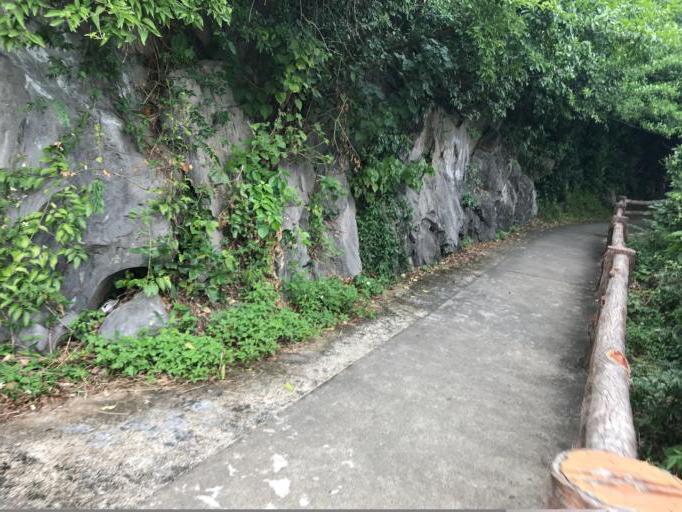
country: VN
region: Hai Phong
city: Cat Ba
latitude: 20.7152
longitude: 107.0526
